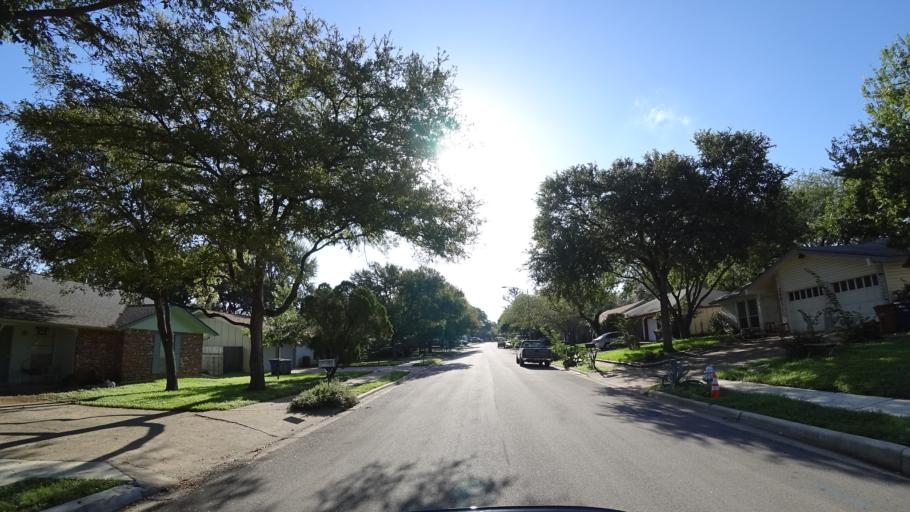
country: US
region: Texas
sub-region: Travis County
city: Rollingwood
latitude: 30.2138
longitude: -97.8100
